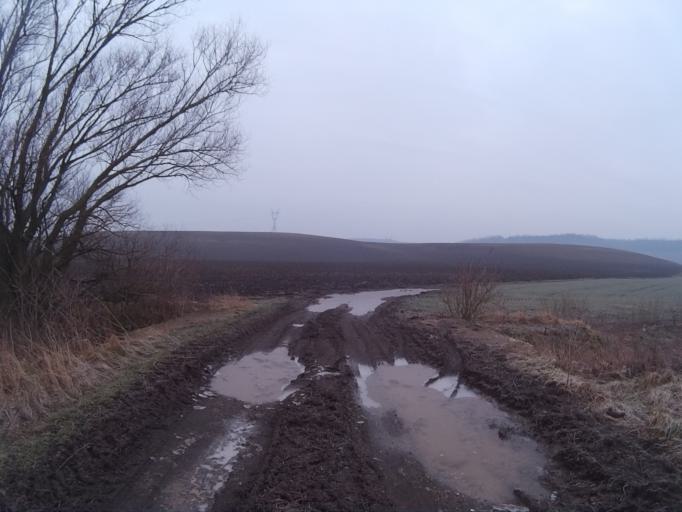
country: HU
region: Komarom-Esztergom
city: Tarjan
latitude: 47.6314
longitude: 18.5025
